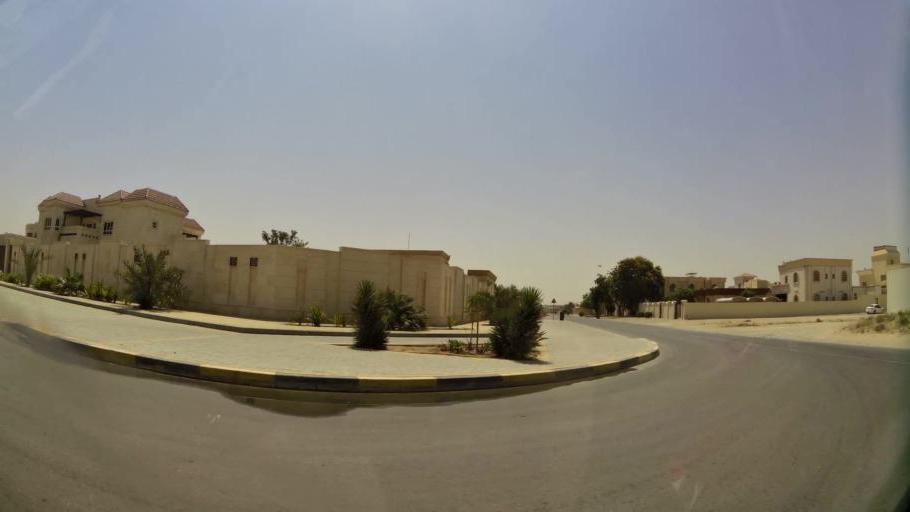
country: AE
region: Ajman
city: Ajman
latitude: 25.4149
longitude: 55.5136
